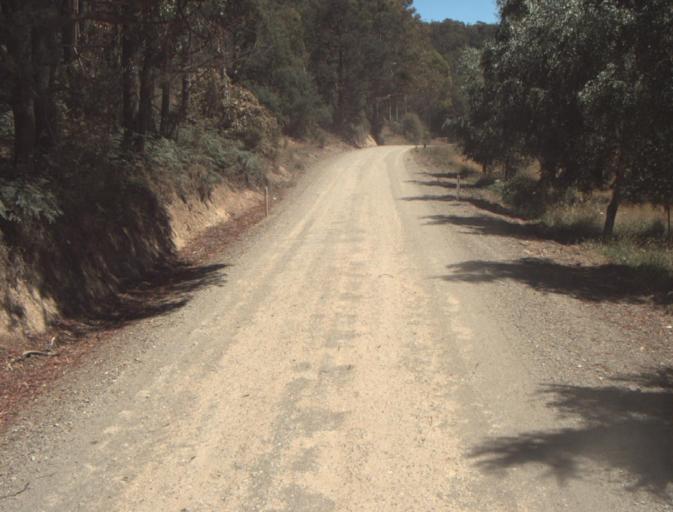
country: AU
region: Tasmania
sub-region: Dorset
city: Scottsdale
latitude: -41.2947
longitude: 147.4010
